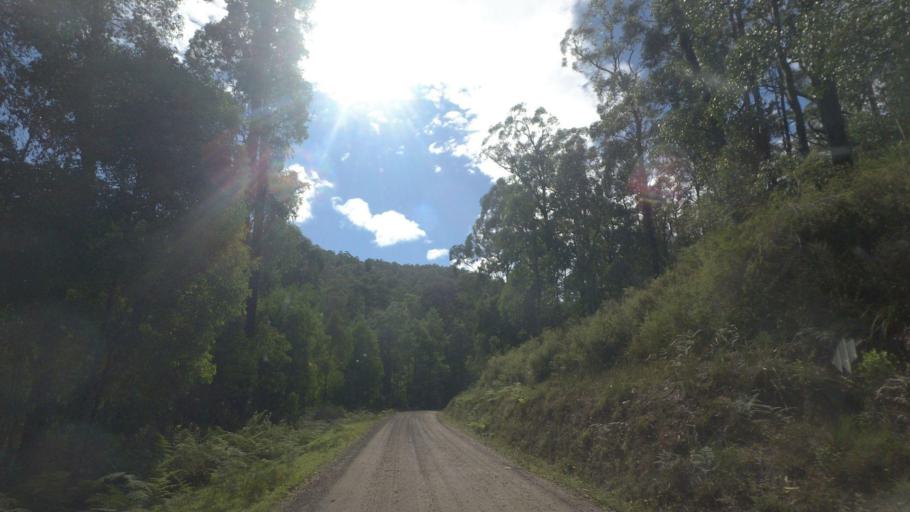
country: AU
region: Victoria
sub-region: Cardinia
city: Bunyip
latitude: -37.9829
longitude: 145.8183
